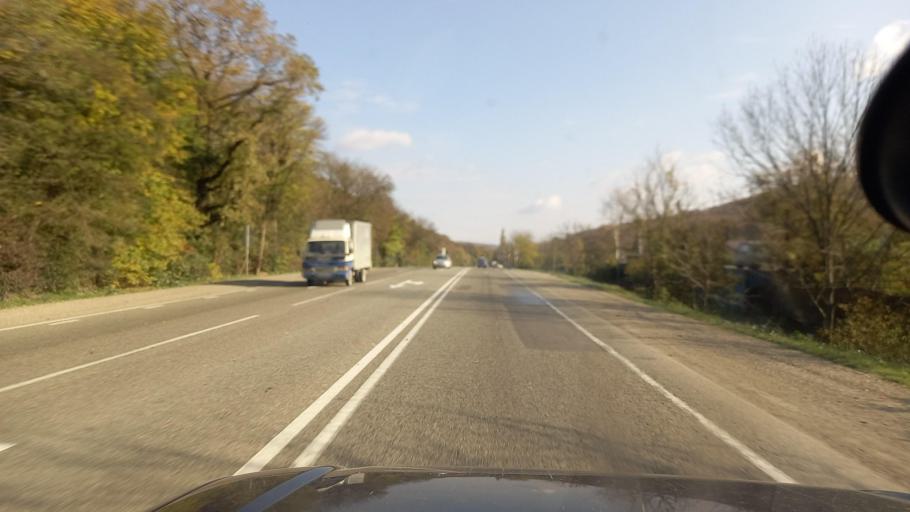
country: RU
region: Krasnodarskiy
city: Verkhnebakanskiy
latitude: 44.8481
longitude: 37.7209
